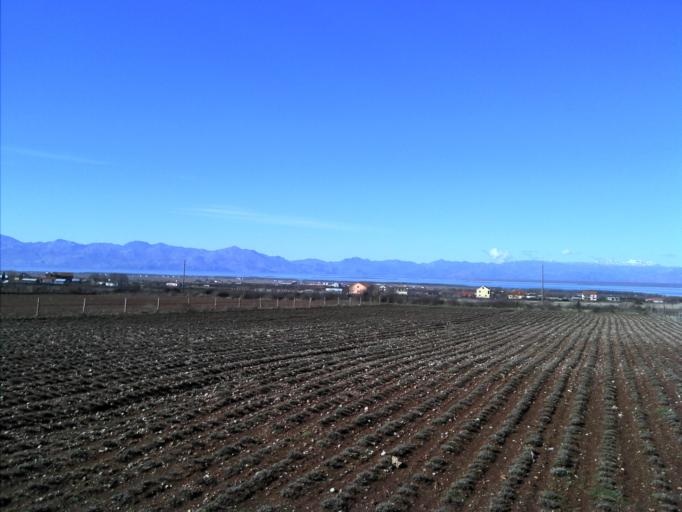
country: AL
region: Shkoder
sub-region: Rrethi i Malesia e Madhe
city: Koplik
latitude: 42.2598
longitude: 19.4282
